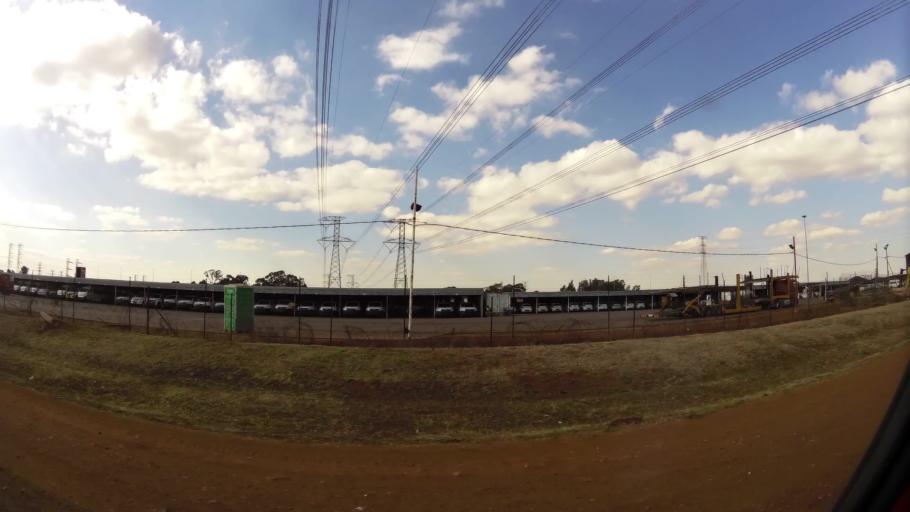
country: ZA
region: Gauteng
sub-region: Ekurhuleni Metropolitan Municipality
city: Tembisa
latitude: -26.0150
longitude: 28.2545
